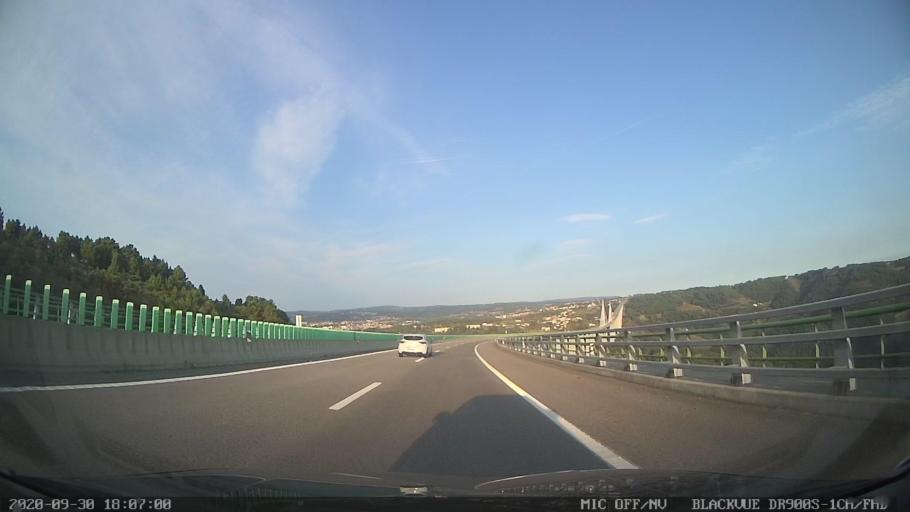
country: PT
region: Vila Real
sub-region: Vila Real
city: Vila Real
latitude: 41.2790
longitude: -7.7660
